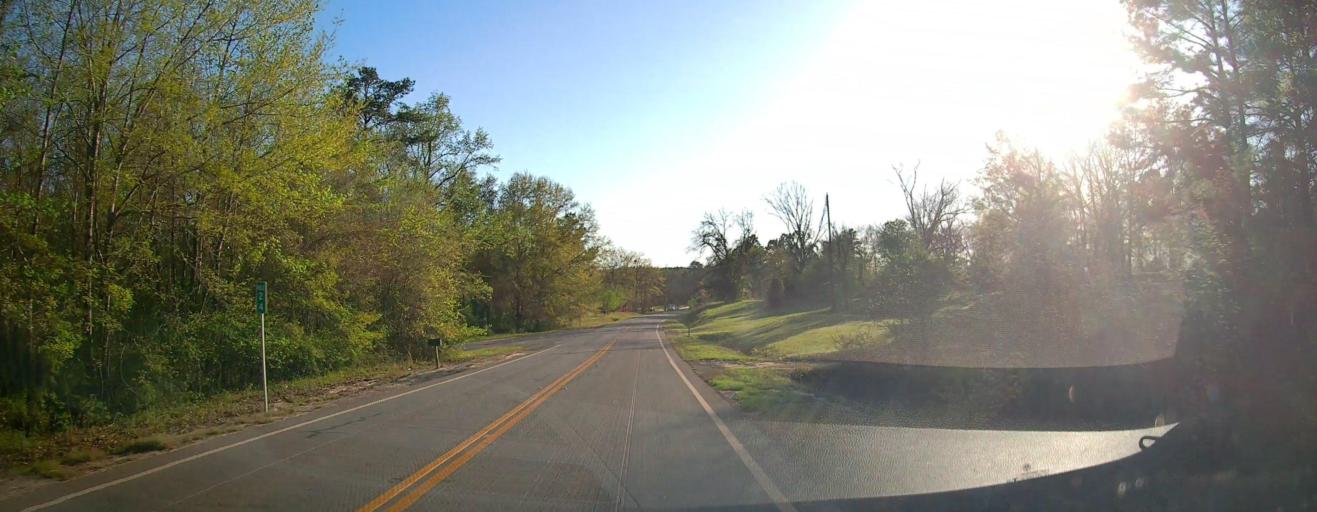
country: US
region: Georgia
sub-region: Wilkinson County
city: Irwinton
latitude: 32.8380
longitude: -83.0713
